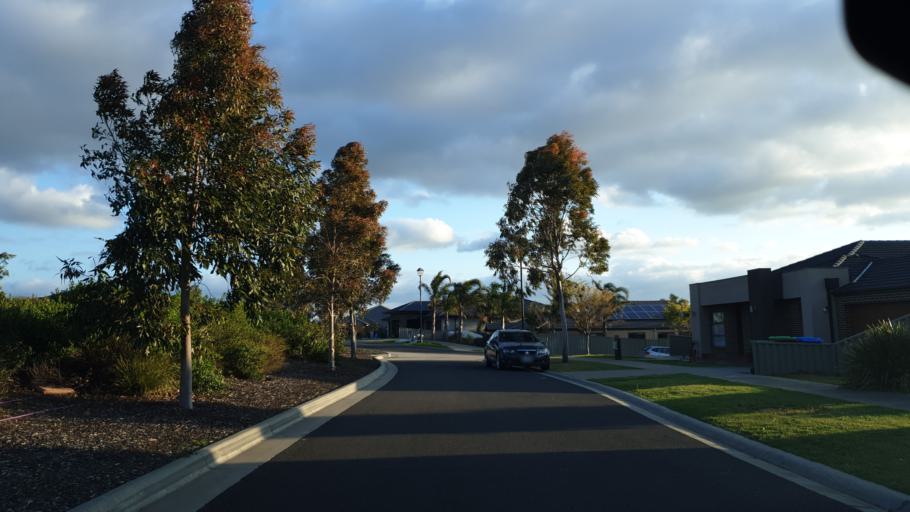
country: AU
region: Victoria
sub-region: Casey
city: Cranbourne East
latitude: -38.1061
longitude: 145.3086
